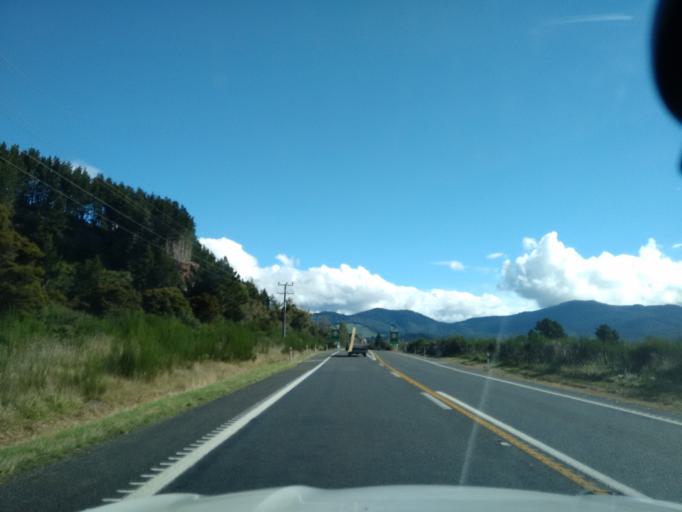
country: NZ
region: Waikato
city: Turangi
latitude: -38.9801
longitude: 175.8259
